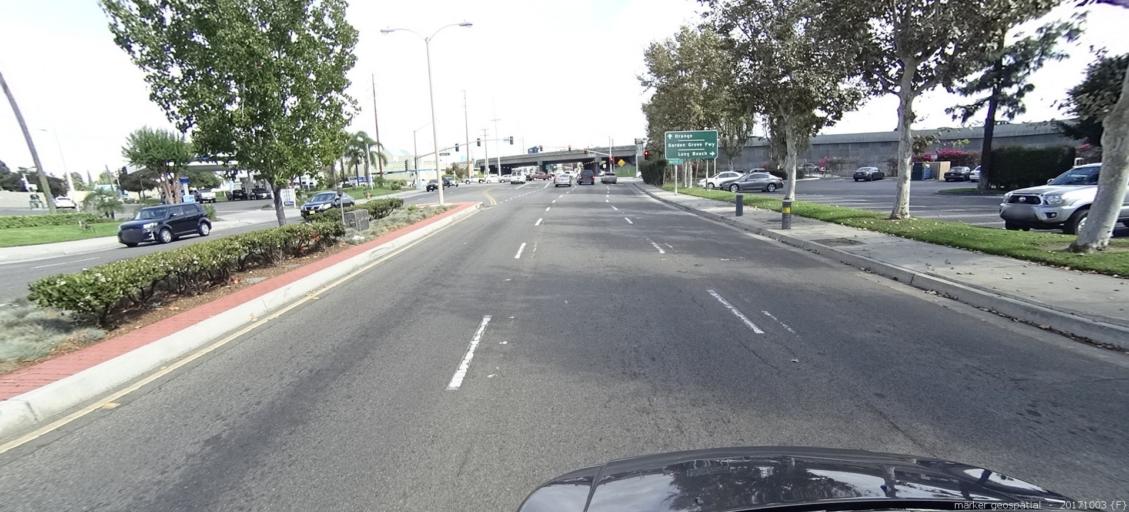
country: US
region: California
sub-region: Orange County
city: Garden Grove
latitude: 33.7744
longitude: -117.9073
